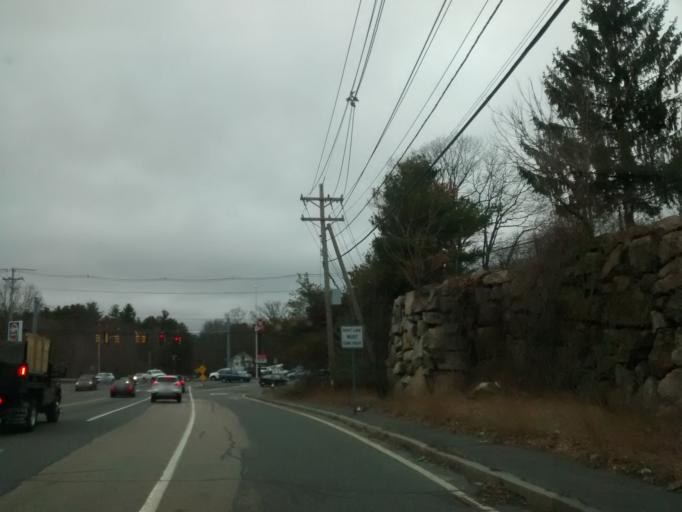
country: US
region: Massachusetts
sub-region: Worcester County
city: Milford
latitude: 42.1622
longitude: -71.5073
